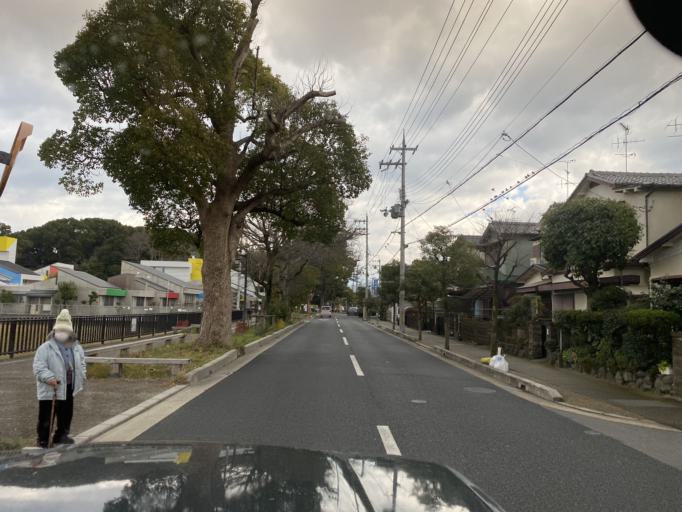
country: JP
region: Kyoto
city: Tanabe
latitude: 34.8409
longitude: 135.7821
